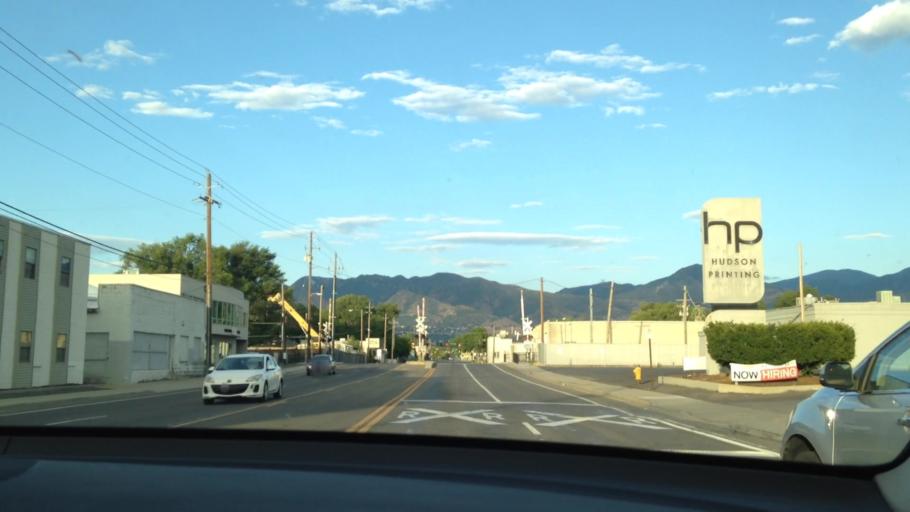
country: US
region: Utah
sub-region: Salt Lake County
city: South Salt Lake
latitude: 40.7335
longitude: -111.8982
